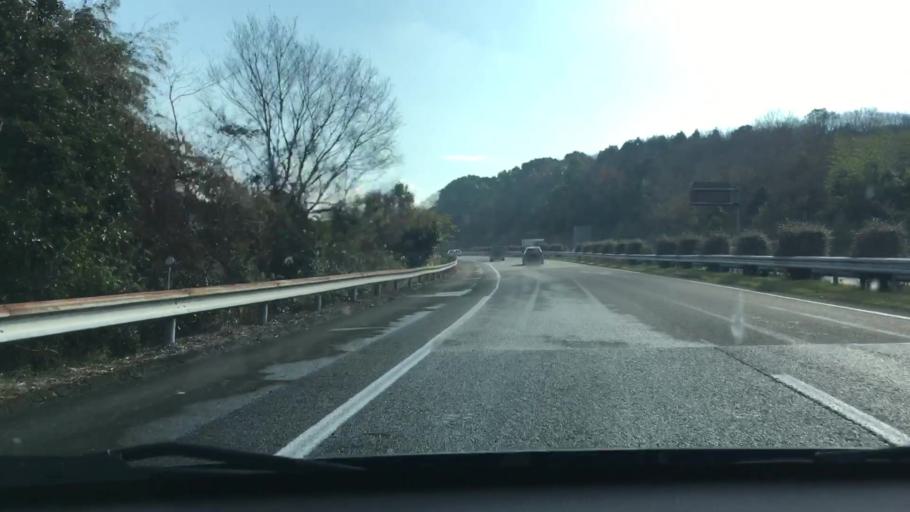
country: JP
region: Kumamoto
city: Matsubase
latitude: 32.6436
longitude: 130.7067
